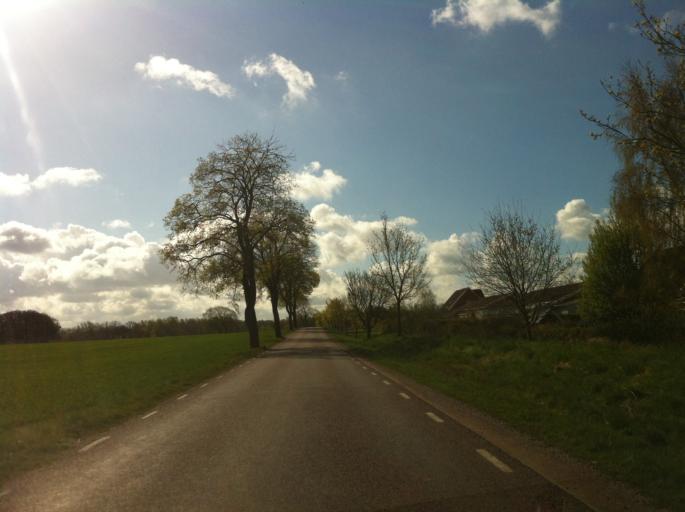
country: SE
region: Skane
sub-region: Eslovs Kommun
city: Stehag
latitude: 55.9072
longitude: 13.3958
